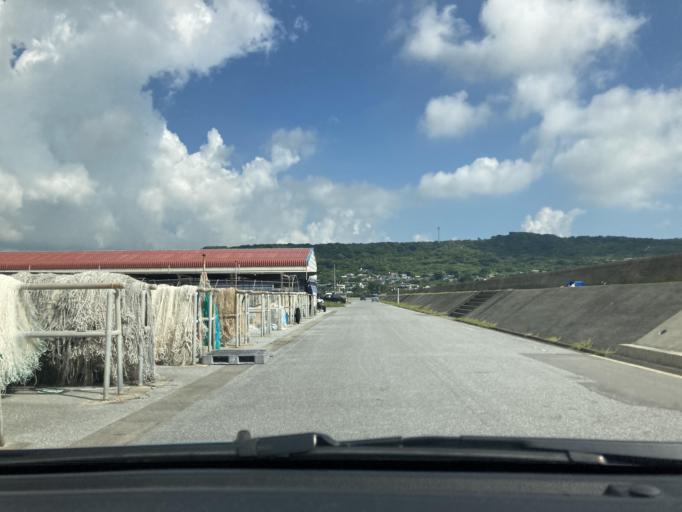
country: JP
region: Okinawa
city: Itoman
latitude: 26.1298
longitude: 127.7767
